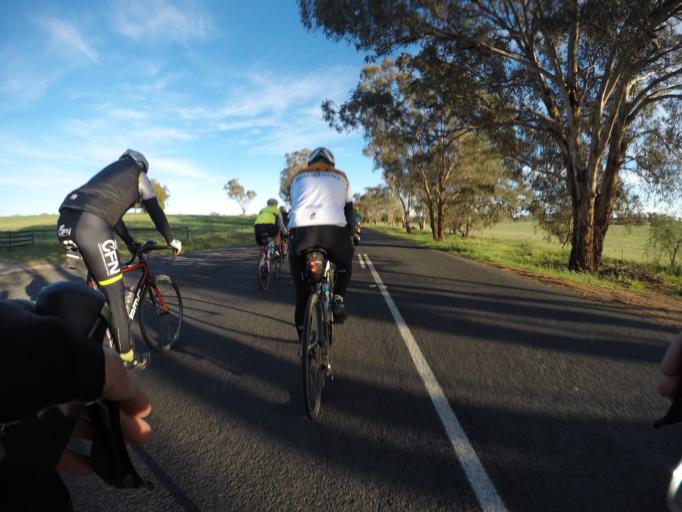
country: AU
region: New South Wales
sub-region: Cabonne
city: Molong
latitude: -33.0308
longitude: 148.8065
